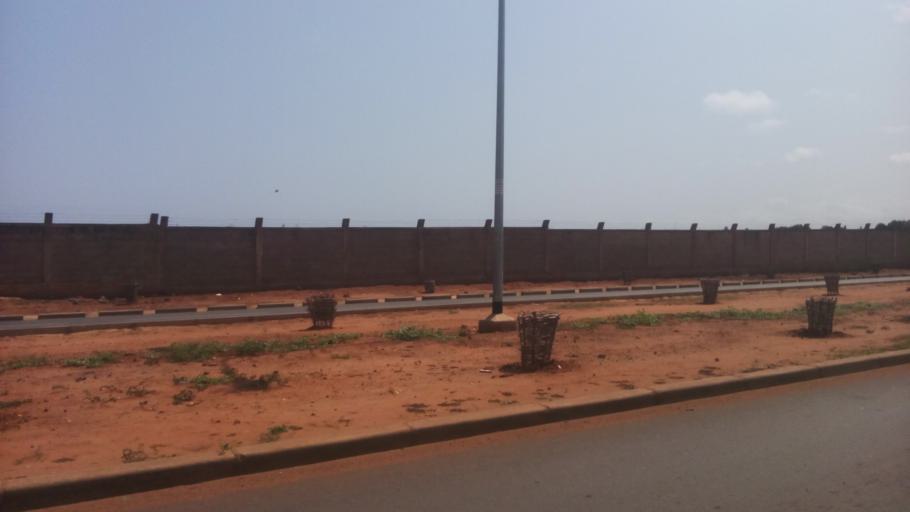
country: TG
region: Maritime
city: Lome
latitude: 6.1875
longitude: 1.2652
